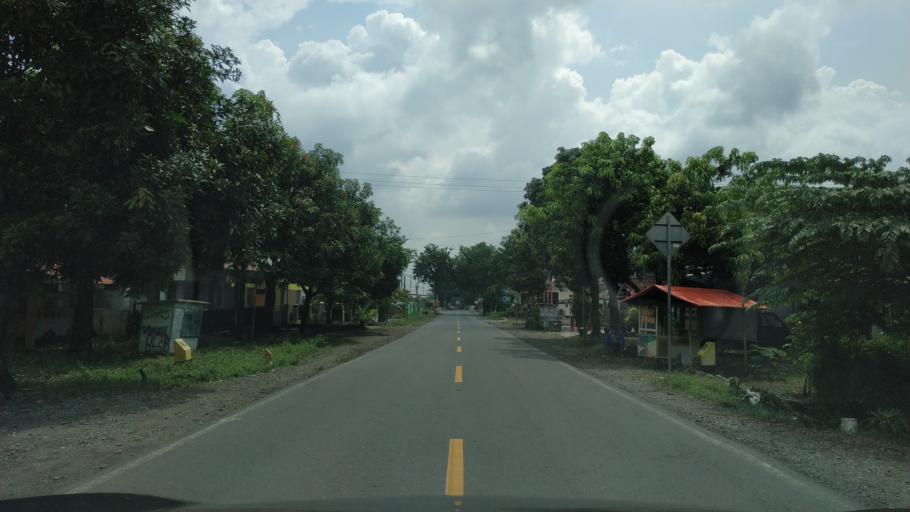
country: ID
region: Central Java
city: Lebaksiu
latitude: -7.0428
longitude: 109.1466
